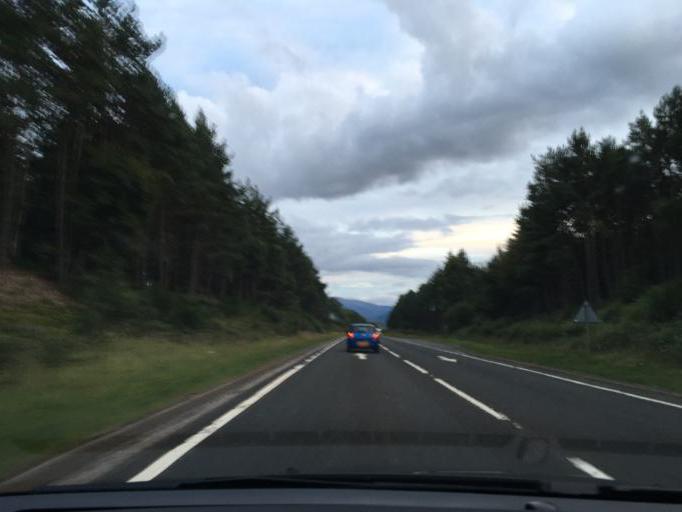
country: GB
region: Scotland
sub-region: Highland
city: Aviemore
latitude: 57.2530
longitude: -3.8076
